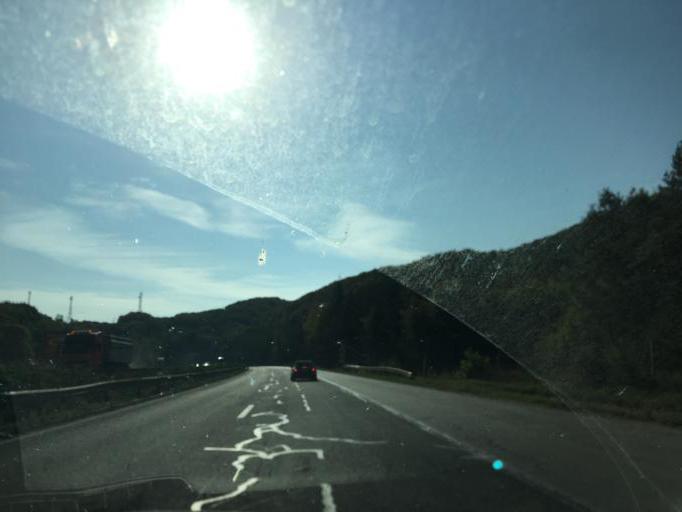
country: BG
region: Sofiya
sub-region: Obshtina Ikhtiman
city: Ikhtiman
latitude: 42.3577
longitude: 23.9085
